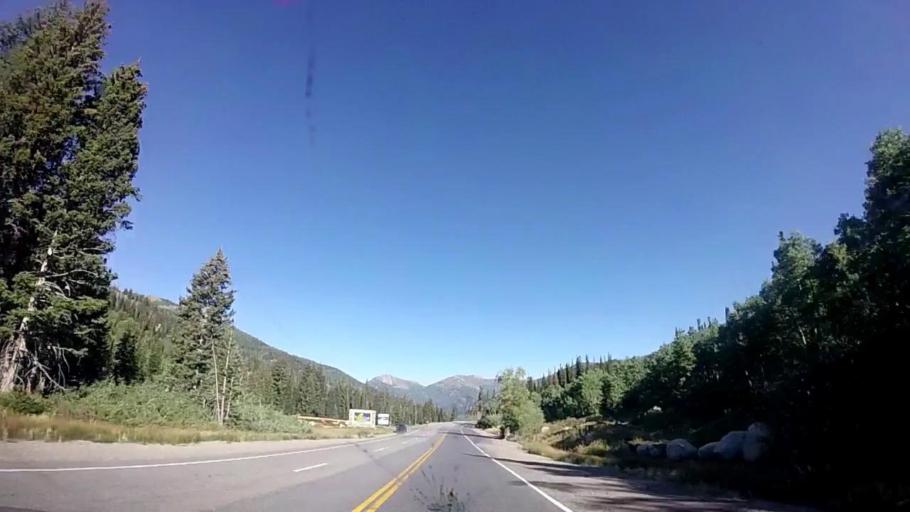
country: US
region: Utah
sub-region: Summit County
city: Snyderville
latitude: 40.6242
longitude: -111.5956
